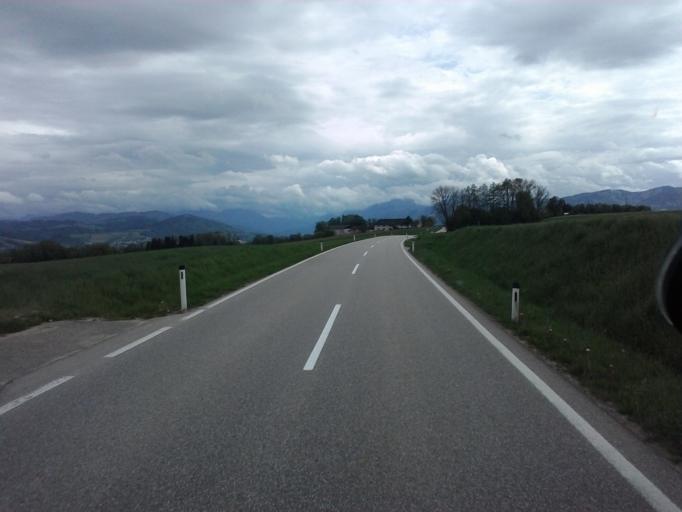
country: AT
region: Upper Austria
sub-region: Politischer Bezirk Kirchdorf an der Krems
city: Kremsmunster
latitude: 47.9897
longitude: 14.0791
